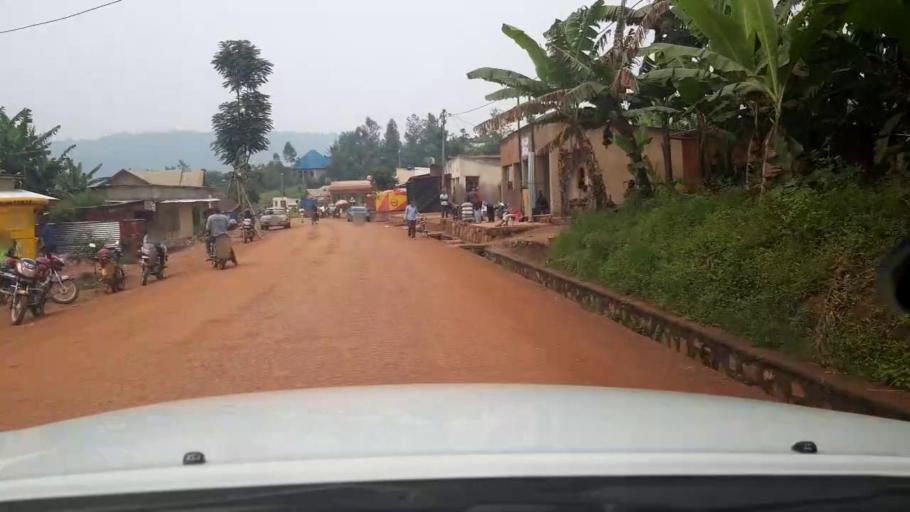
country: RW
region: Kigali
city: Kigali
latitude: -1.9021
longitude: 29.9695
